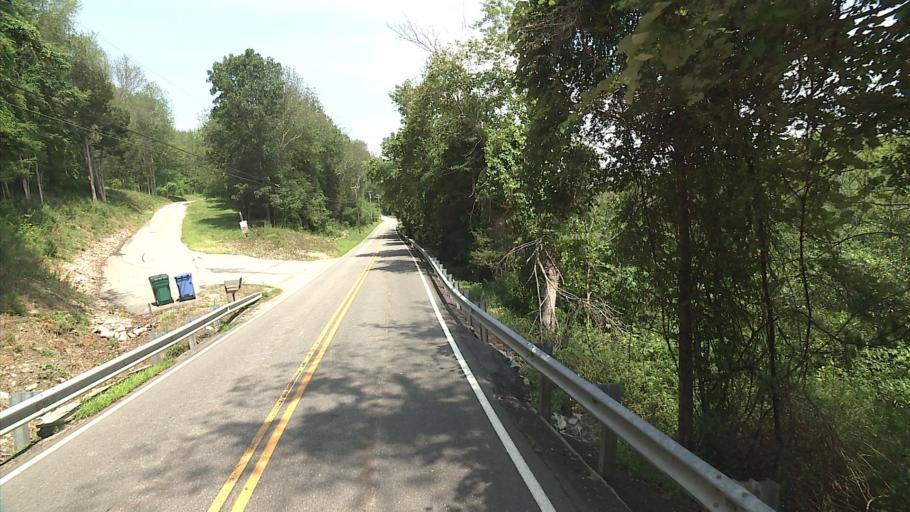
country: US
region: Connecticut
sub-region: Windham County
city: Moosup
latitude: 41.7546
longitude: -71.8533
